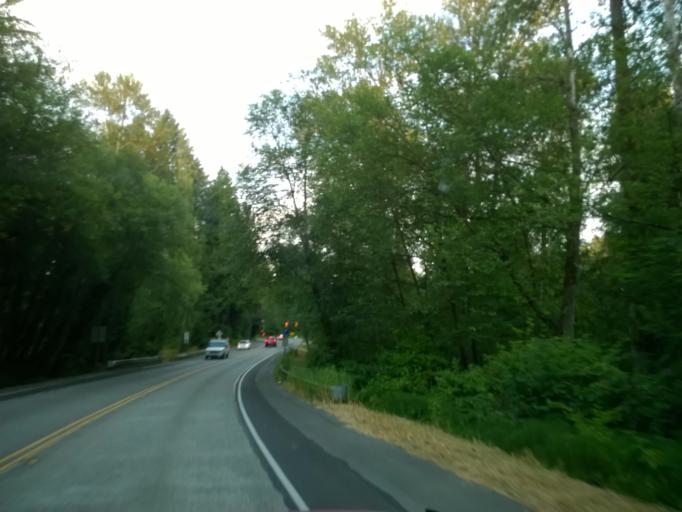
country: US
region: Washington
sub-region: King County
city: Cottage Lake
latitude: 47.7156
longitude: -122.0902
